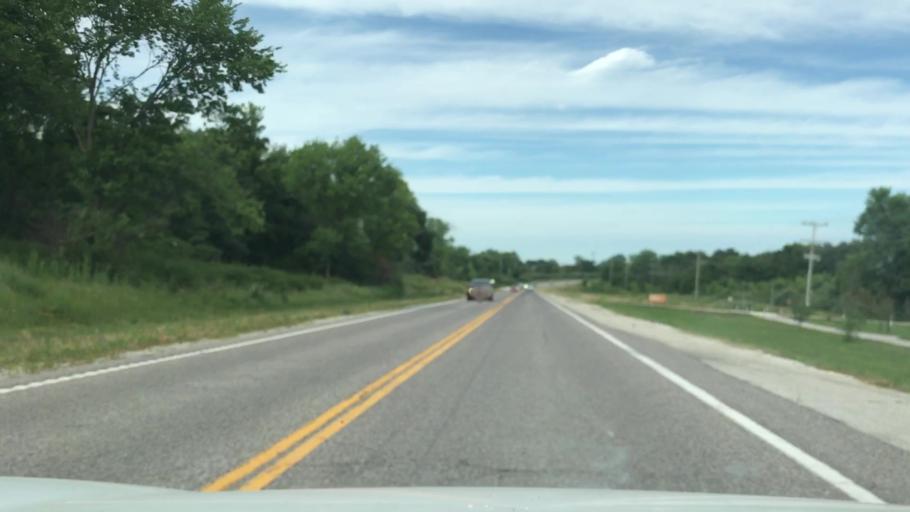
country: US
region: Missouri
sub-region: Saint Charles County
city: Weldon Spring
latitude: 38.7057
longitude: -90.7057
